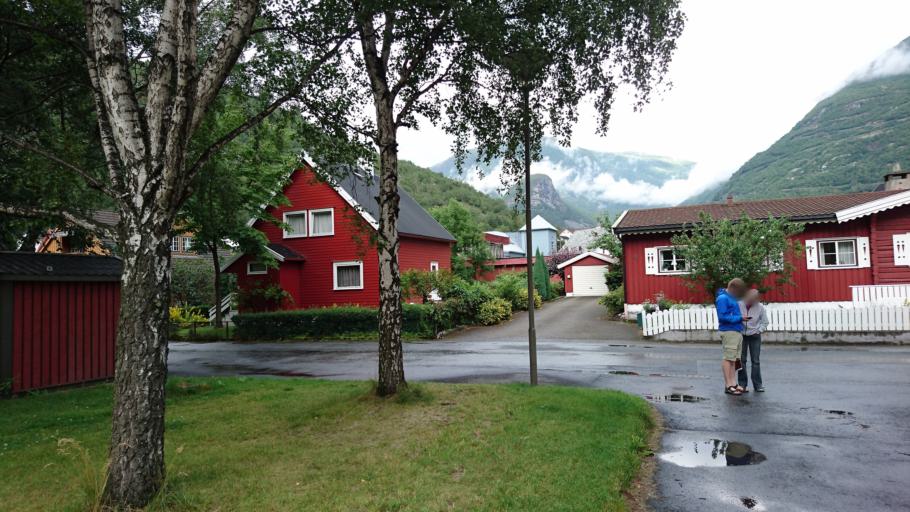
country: NO
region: Sogn og Fjordane
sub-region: Ardal
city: Farnes
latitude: 61.3106
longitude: 7.8016
